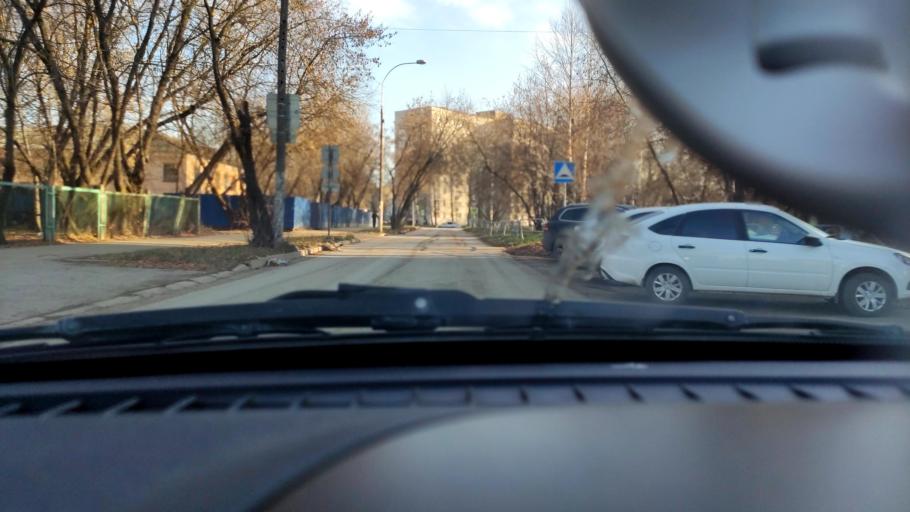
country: RU
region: Perm
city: Perm
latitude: 57.9748
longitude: 56.2384
